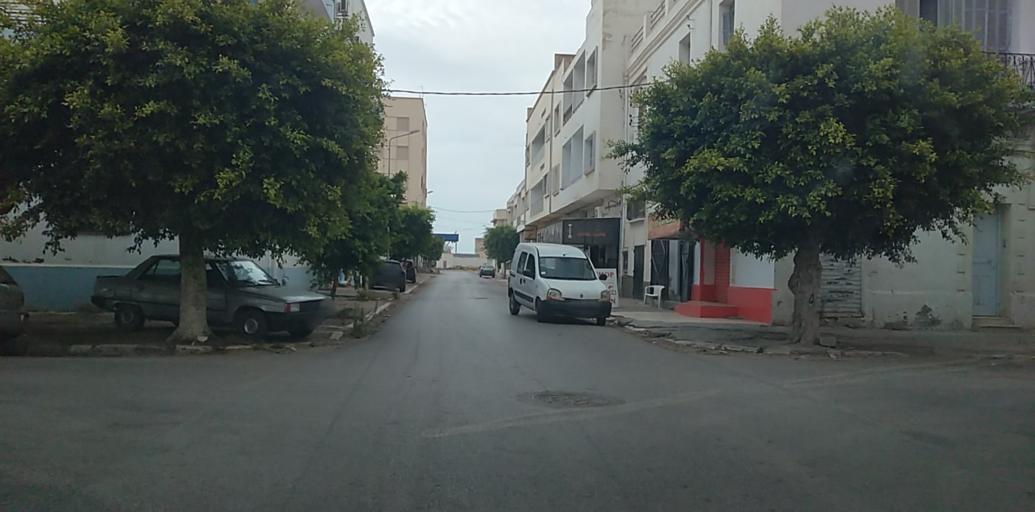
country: TN
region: Safaqis
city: Sfax
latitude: 34.7331
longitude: 10.7674
